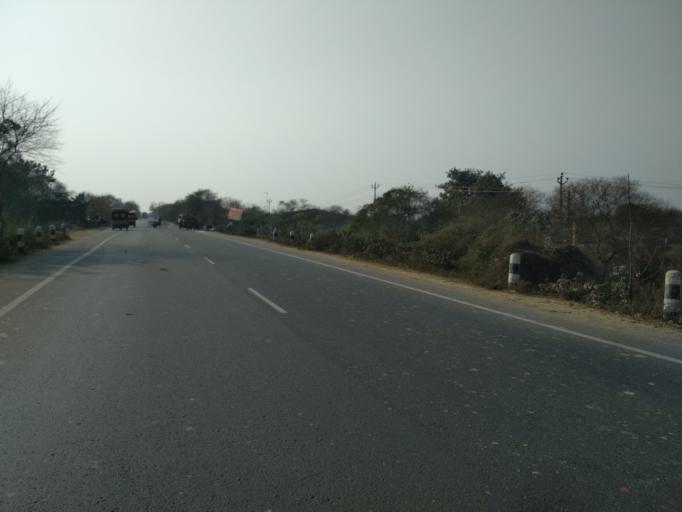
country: IN
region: Bihar
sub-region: Khagaria
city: Khagaria
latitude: 25.5075
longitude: 86.5510
